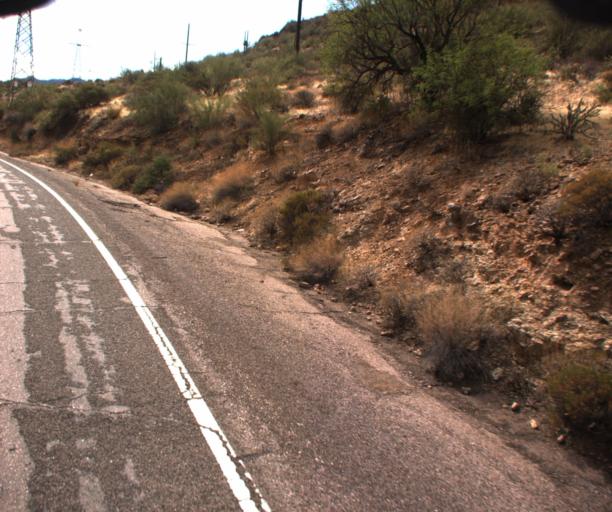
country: US
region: Arizona
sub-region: Pinal County
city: Apache Junction
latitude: 33.5159
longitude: -111.4575
